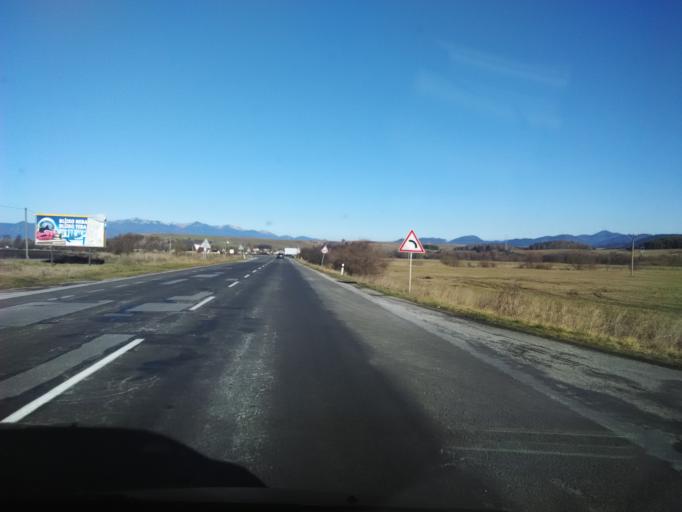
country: SK
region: Zilinsky
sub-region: Okres Martin
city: Martin
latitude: 48.9627
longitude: 18.9050
